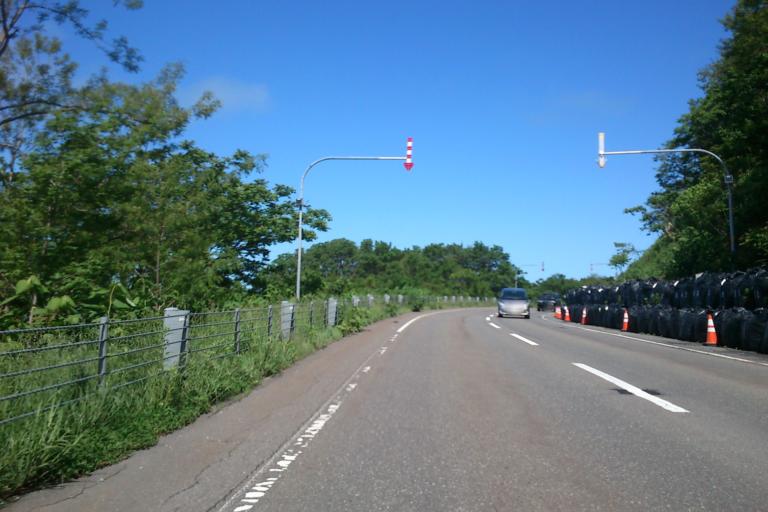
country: JP
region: Hokkaido
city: Ishikari
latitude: 43.4853
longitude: 141.3854
